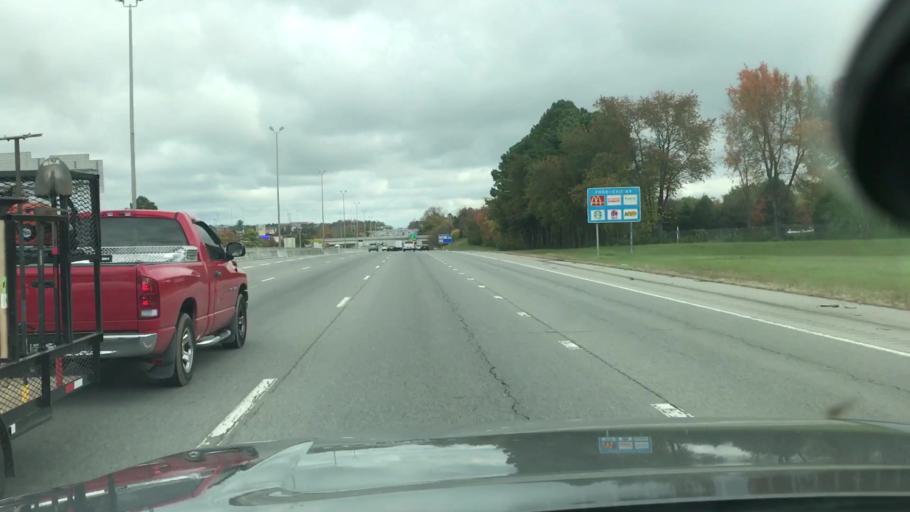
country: US
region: Tennessee
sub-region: Williamson County
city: Franklin
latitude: 35.9559
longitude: -86.8111
